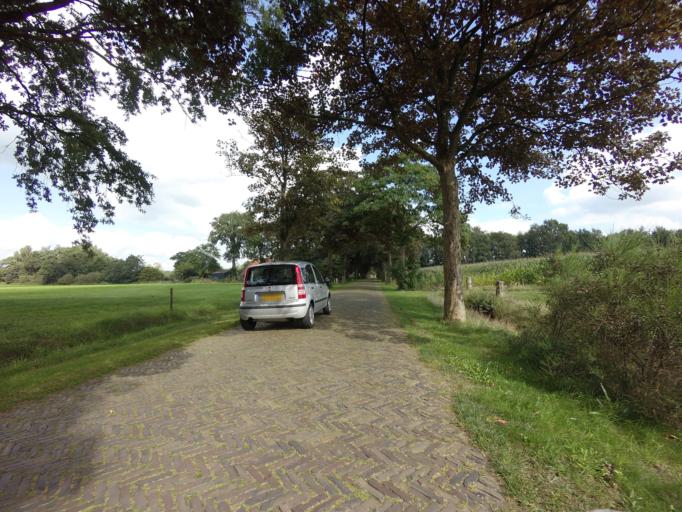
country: NL
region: Friesland
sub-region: Gemeente Heerenveen
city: Jubbega
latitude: 52.9827
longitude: 6.2685
